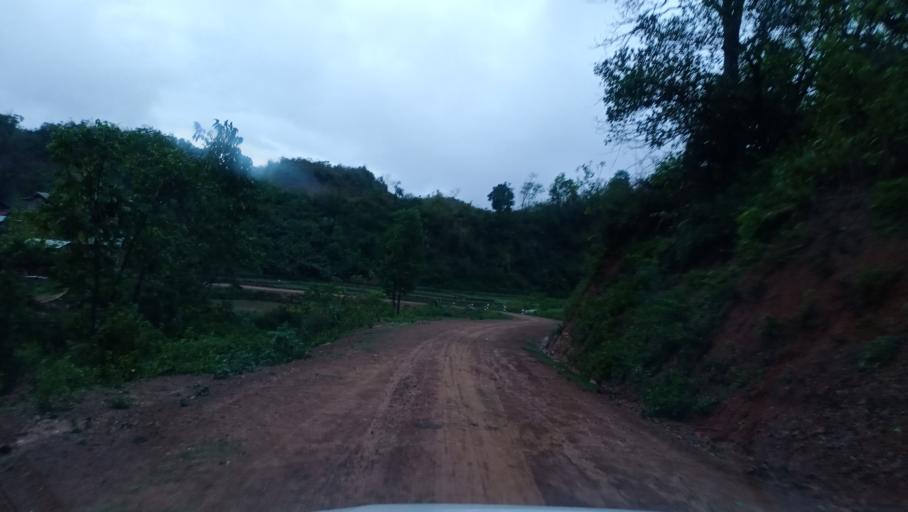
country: VN
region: Huyen Dien Bien
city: Dien Bien Phu
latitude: 21.3400
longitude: 102.7206
